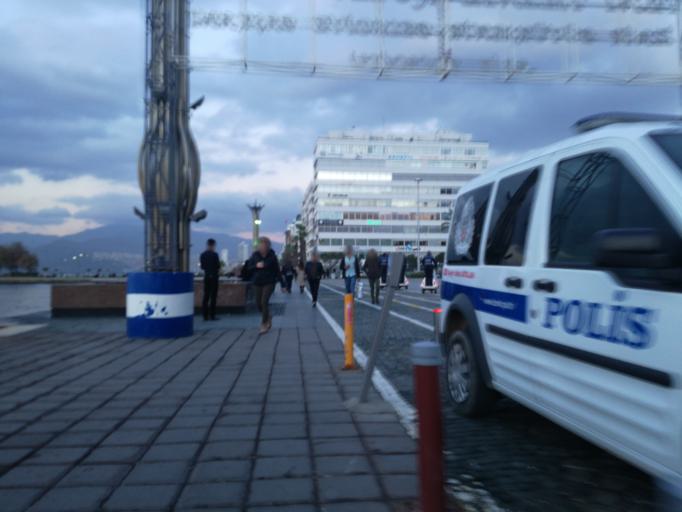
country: TR
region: Izmir
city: Izmir
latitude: 38.4287
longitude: 27.1335
